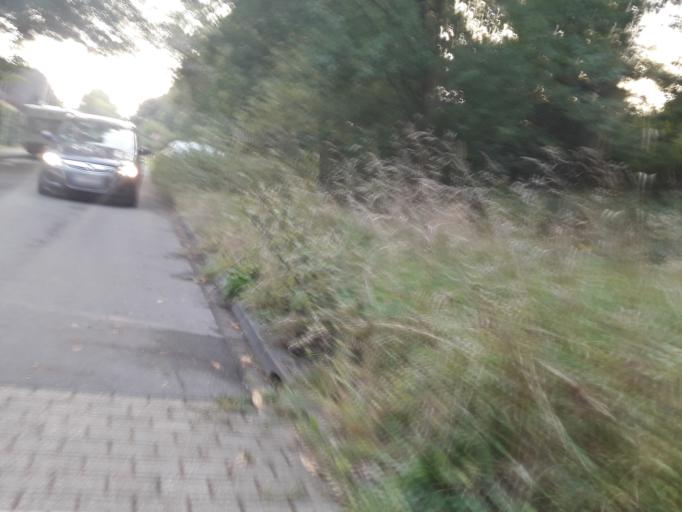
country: DE
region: North Rhine-Westphalia
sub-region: Regierungsbezirk Munster
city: Muenster
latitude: 51.9289
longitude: 7.6560
